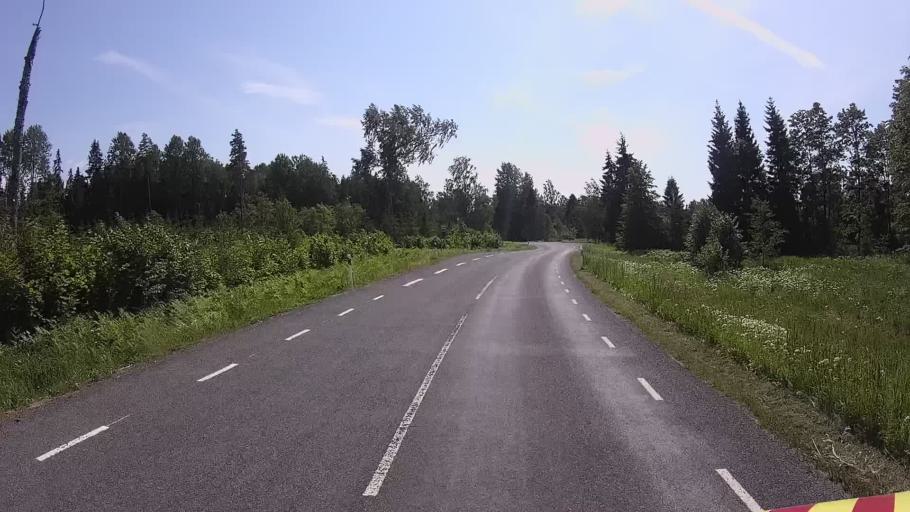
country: EE
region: Viljandimaa
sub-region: Karksi vald
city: Karksi-Nuia
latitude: 58.0318
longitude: 25.5422
